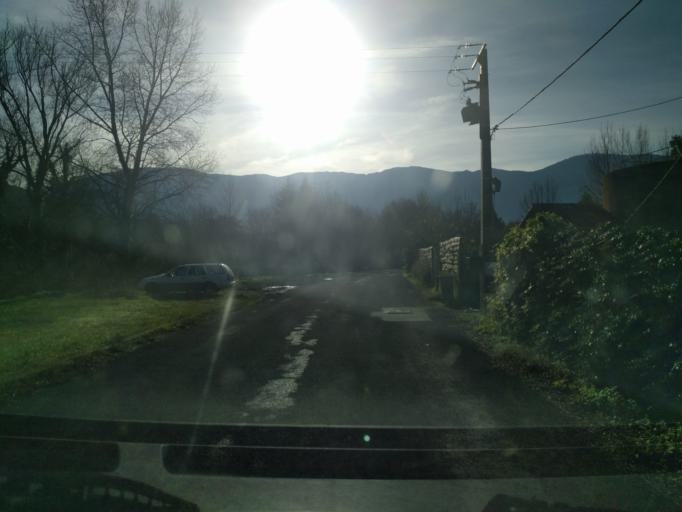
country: FR
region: Languedoc-Roussillon
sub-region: Departement de l'Aude
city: Quillan
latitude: 42.8816
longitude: 2.1892
